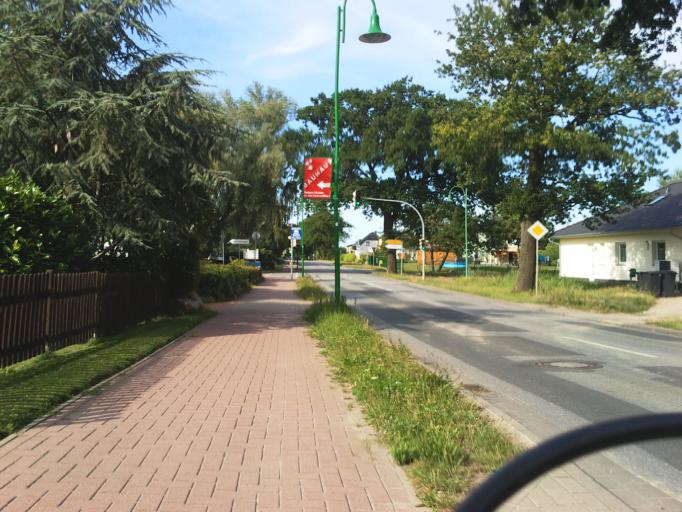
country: DE
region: Mecklenburg-Vorpommern
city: Kritzmow
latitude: 54.0551
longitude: 12.0536
